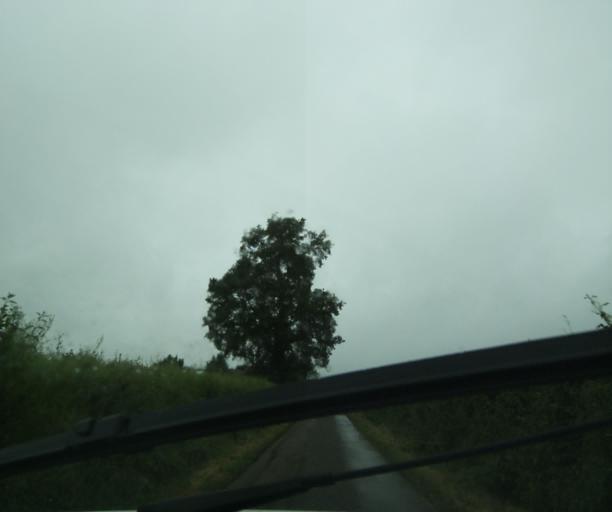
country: FR
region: Bourgogne
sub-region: Departement de Saone-et-Loire
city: Charolles
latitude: 46.3997
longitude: 4.2379
